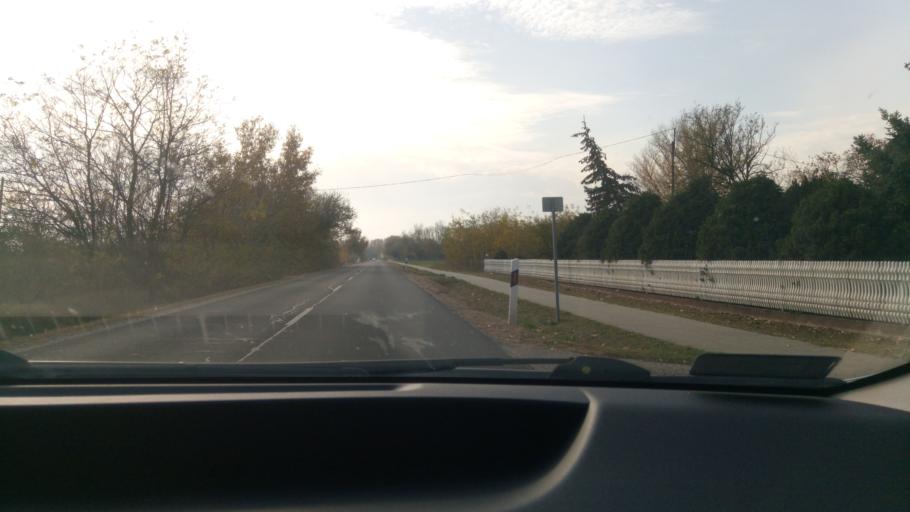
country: HU
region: Bacs-Kiskun
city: Jaszszentlaszlo
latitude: 46.5494
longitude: 19.7460
